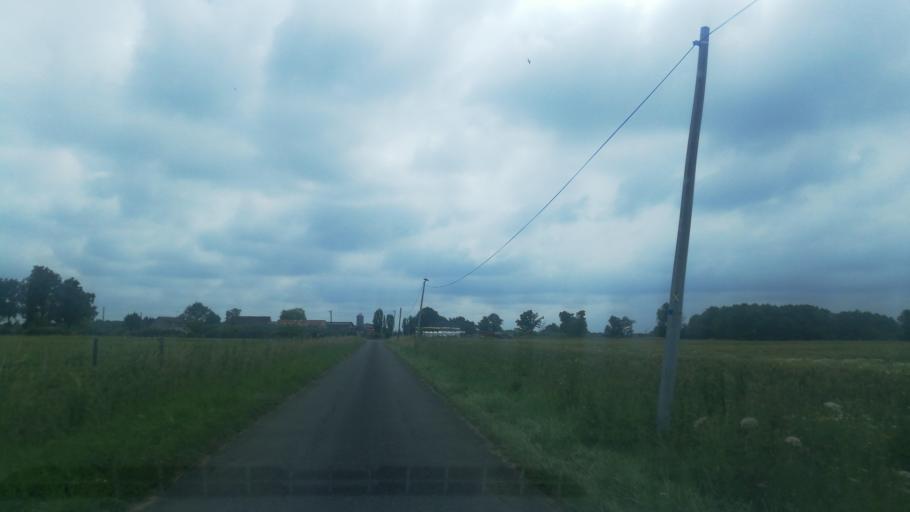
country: FR
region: Centre
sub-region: Departement du Loir-et-Cher
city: Saint-Romain-sur-Cher
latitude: 47.3377
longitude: 1.4508
